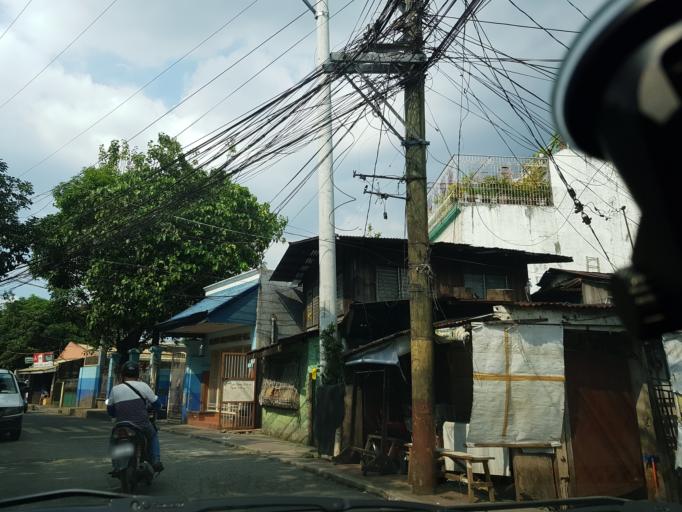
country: PH
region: Calabarzon
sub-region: Province of Rizal
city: Pateros
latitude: 14.5629
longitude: 121.0900
